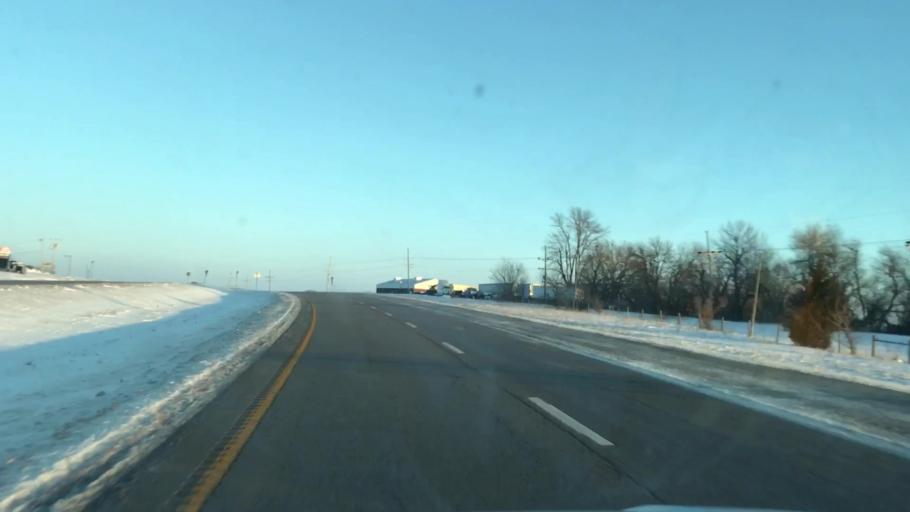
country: US
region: Missouri
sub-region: Clinton County
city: Cameron
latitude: 39.7552
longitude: -94.3399
